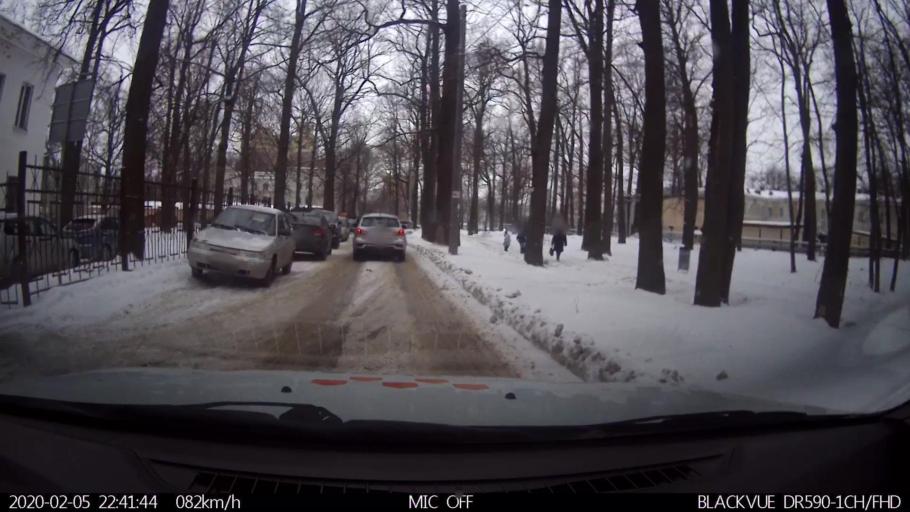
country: RU
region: Nizjnij Novgorod
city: Imeni Stepana Razina
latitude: 54.7201
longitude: 44.3439
